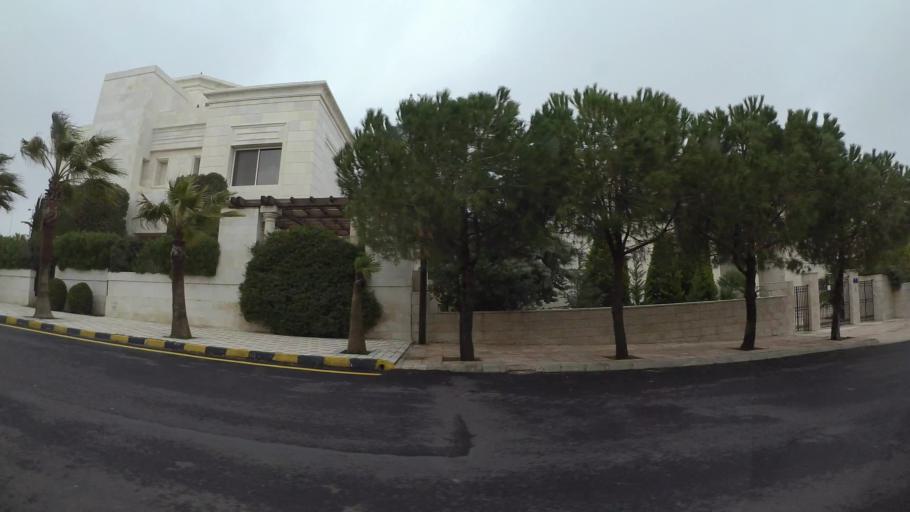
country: JO
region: Amman
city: Al Bunayyat ash Shamaliyah
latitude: 31.9373
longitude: 35.8791
